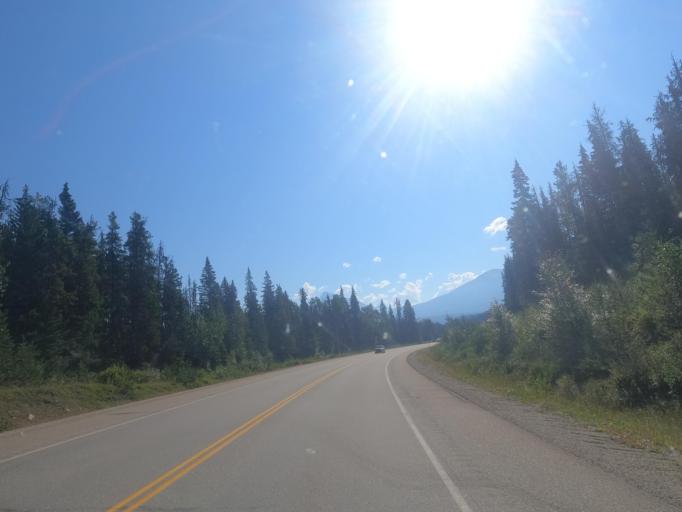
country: CA
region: Alberta
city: Jasper Park Lodge
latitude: 52.8623
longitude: -118.6441
